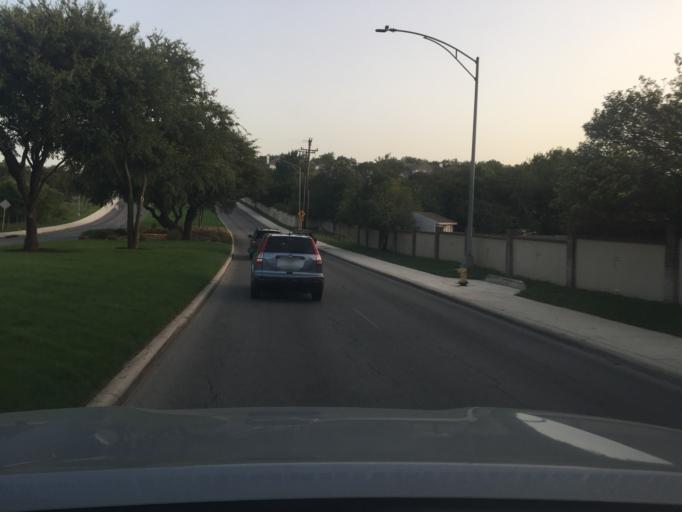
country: US
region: Texas
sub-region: Bexar County
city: Hollywood Park
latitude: 29.6383
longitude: -98.4952
